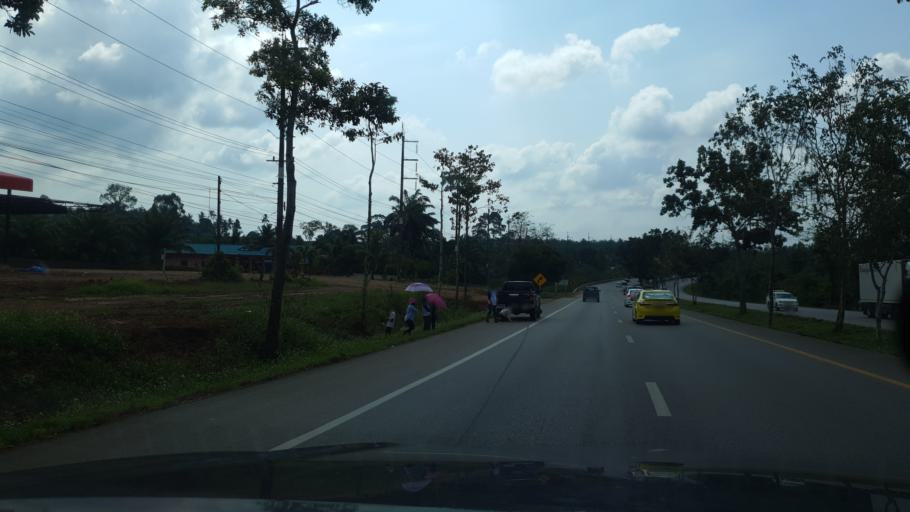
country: TH
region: Chumphon
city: Tha Sae
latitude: 10.6290
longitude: 99.1777
